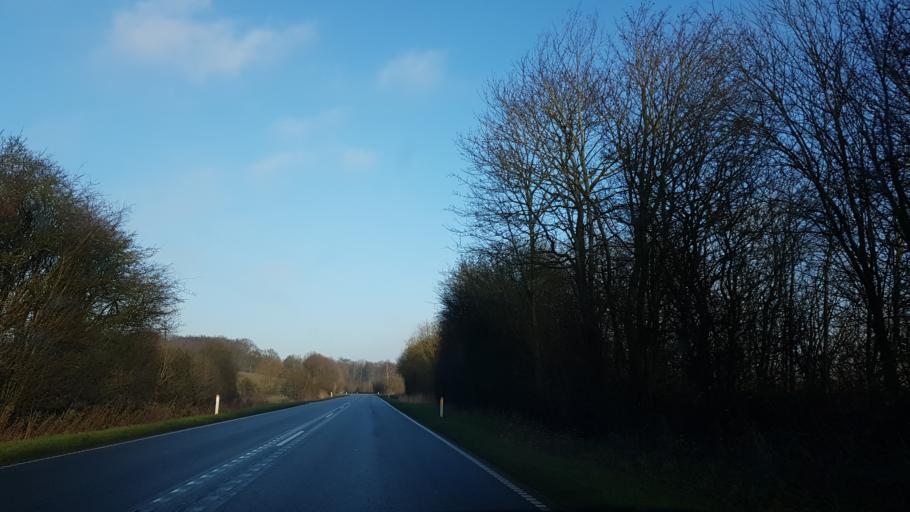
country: DK
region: South Denmark
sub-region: Haderslev Kommune
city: Haderslev
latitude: 55.1856
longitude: 9.4070
